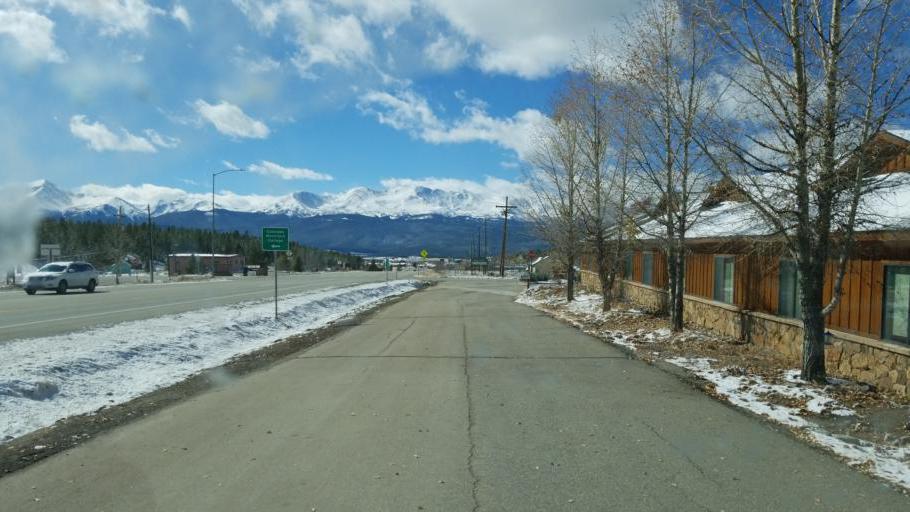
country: US
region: Colorado
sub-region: Lake County
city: Leadville
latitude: 39.2406
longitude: -106.3015
